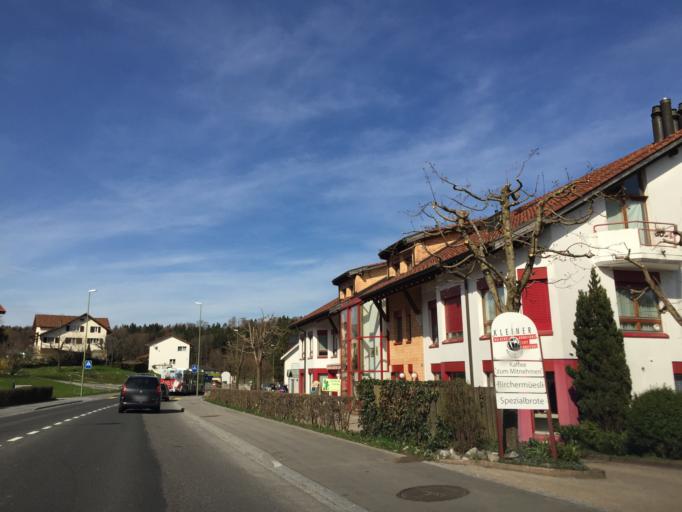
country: CH
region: Zurich
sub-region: Bezirk Horgen
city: Horgen / Allmend
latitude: 47.2165
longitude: 8.6112
